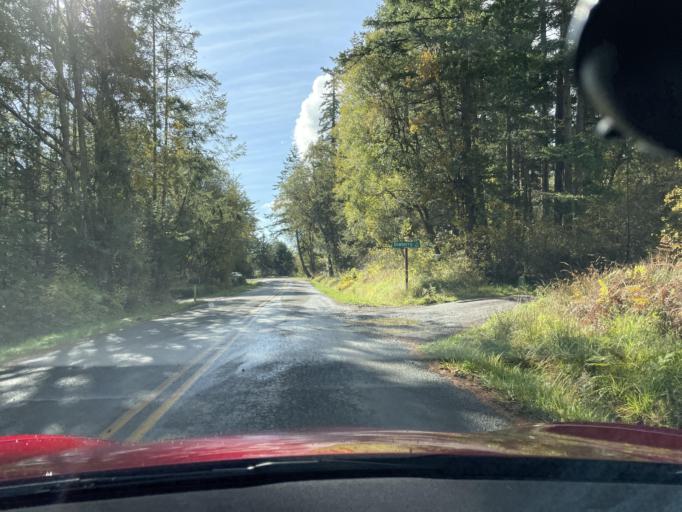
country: US
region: Washington
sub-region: San Juan County
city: Friday Harbor
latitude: 48.5083
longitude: -123.0231
